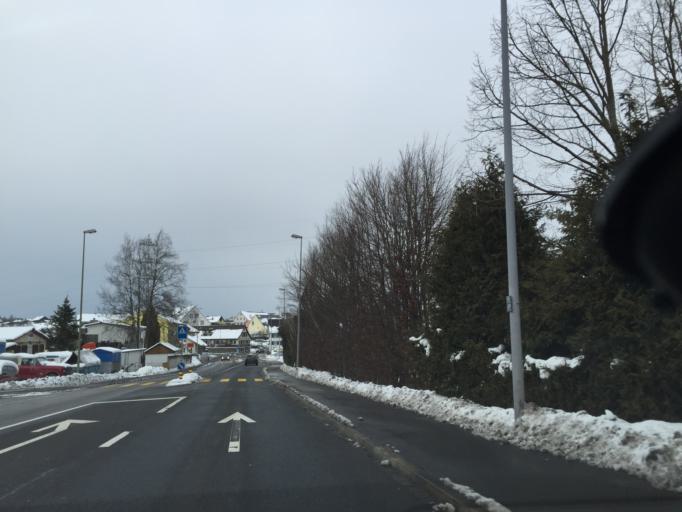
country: CH
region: Zurich
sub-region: Bezirk Horgen
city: Richterswil / Burghalde
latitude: 47.1908
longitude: 8.6764
